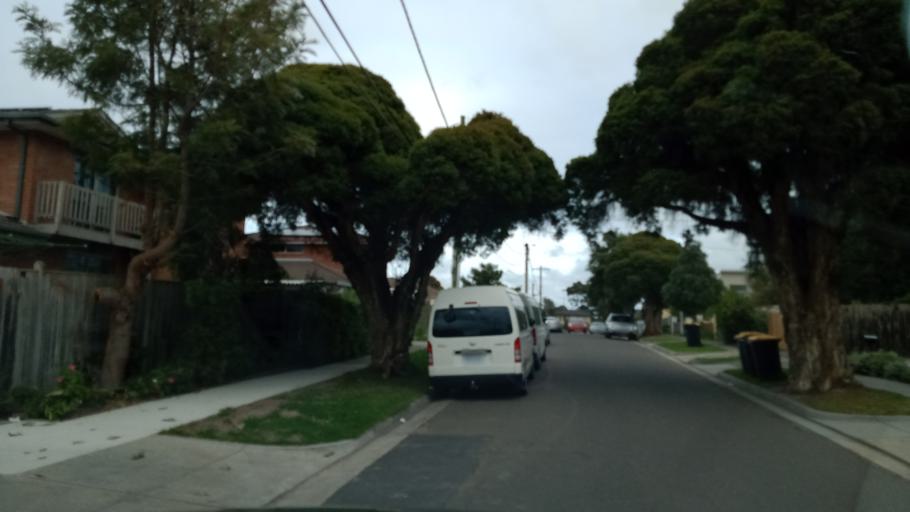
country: AU
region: Victoria
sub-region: Casey
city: Doveton
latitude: -37.9935
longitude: 145.2246
